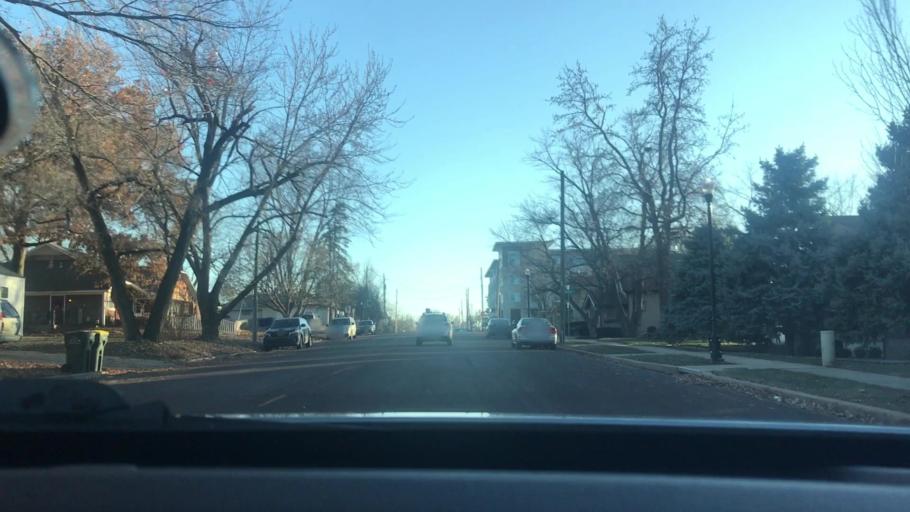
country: US
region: Kansas
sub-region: Johnson County
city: Overland Park
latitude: 38.9871
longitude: -94.6736
